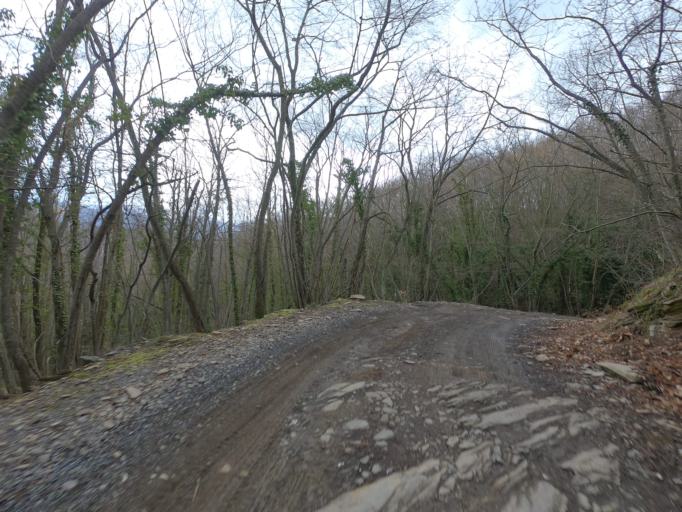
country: IT
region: Liguria
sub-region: Provincia di Imperia
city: Pietrabruna
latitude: 43.9129
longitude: 7.8876
